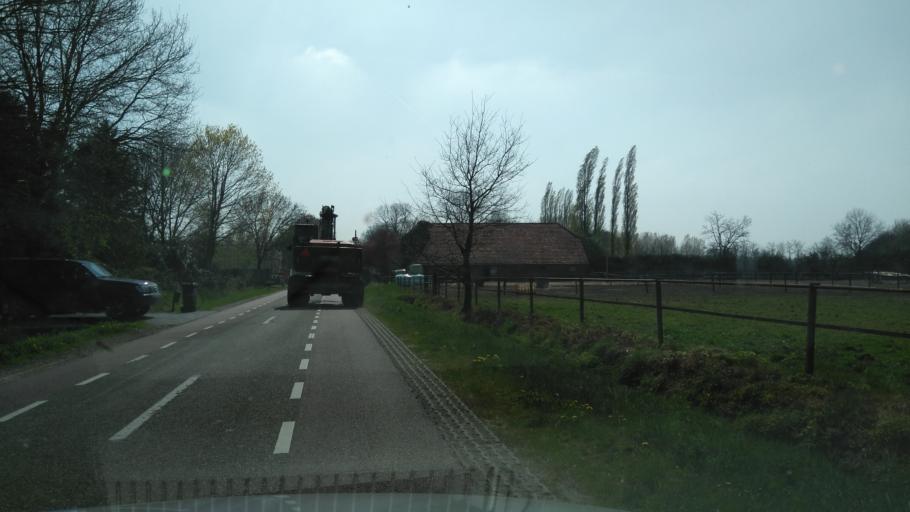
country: BE
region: Flanders
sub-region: Provincie Antwerpen
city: Baarle-Hertog
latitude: 51.4153
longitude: 4.9018
